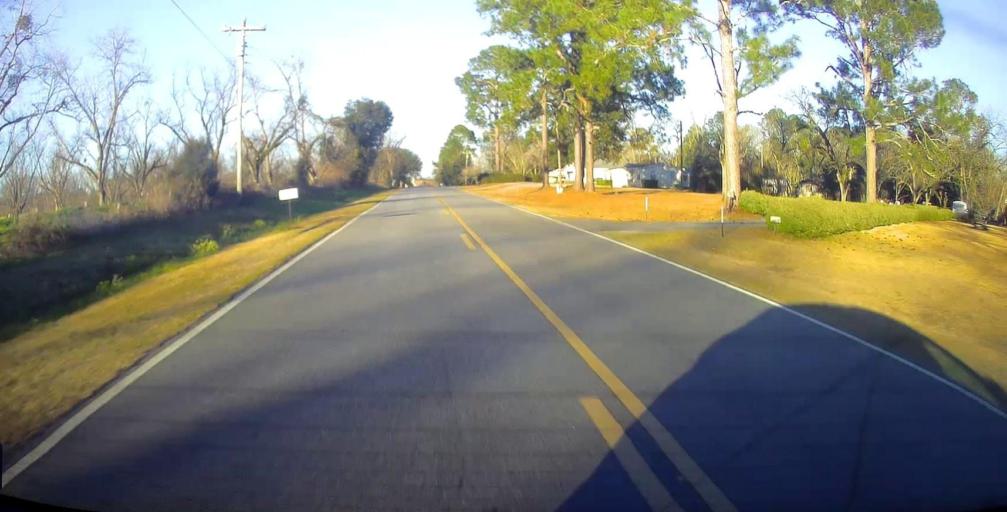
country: US
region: Georgia
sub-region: Dougherty County
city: Albany
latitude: 31.5152
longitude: -84.2338
